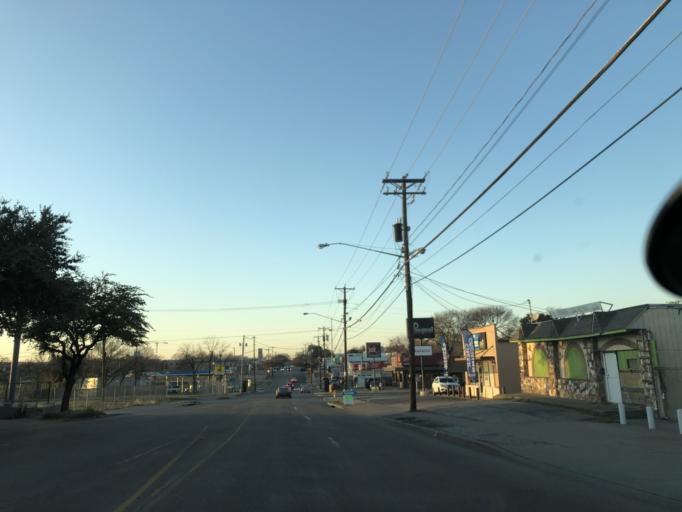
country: US
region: Texas
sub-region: Dallas County
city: Dallas
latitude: 32.8098
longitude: -96.8206
